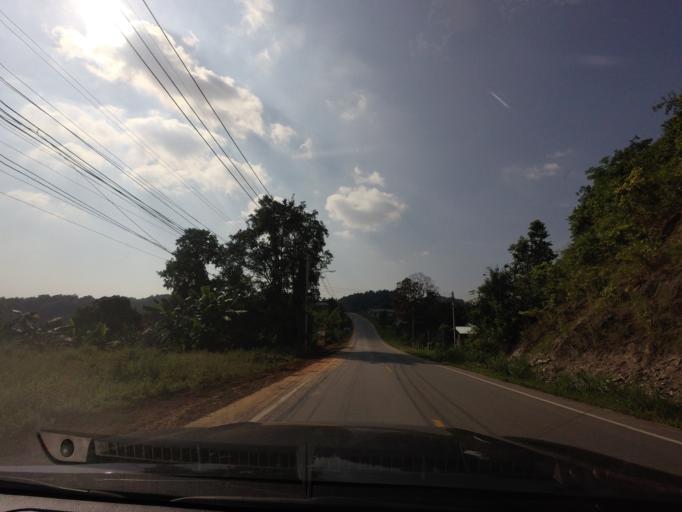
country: TH
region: Nan
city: Santi Suk
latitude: 18.9156
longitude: 100.8802
